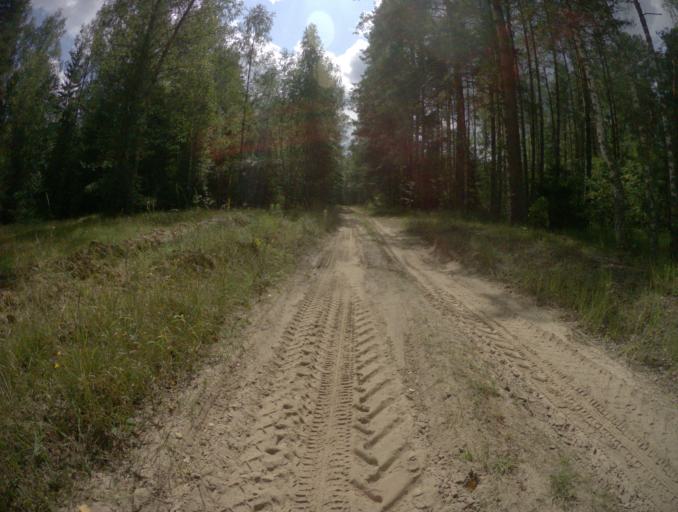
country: RU
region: Vladimir
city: Vorsha
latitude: 55.9619
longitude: 40.1558
